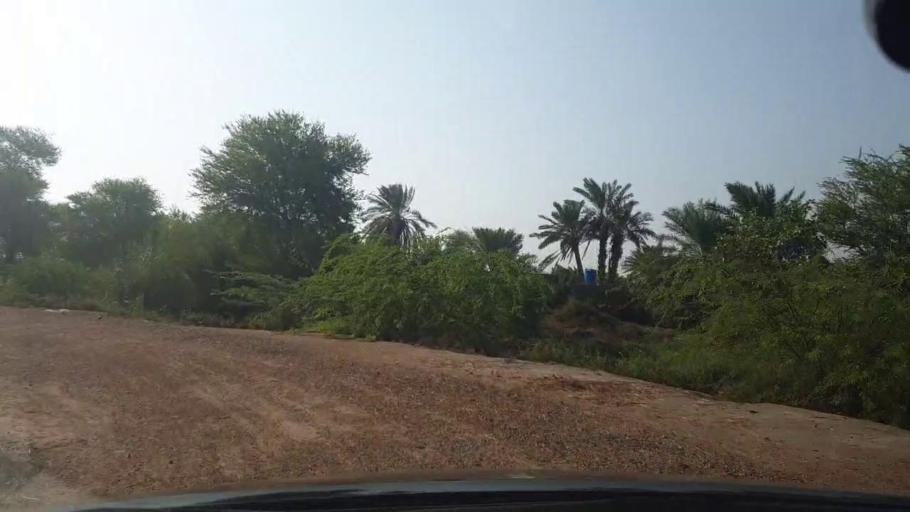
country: PK
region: Sindh
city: Tando Bago
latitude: 24.6483
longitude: 69.1477
